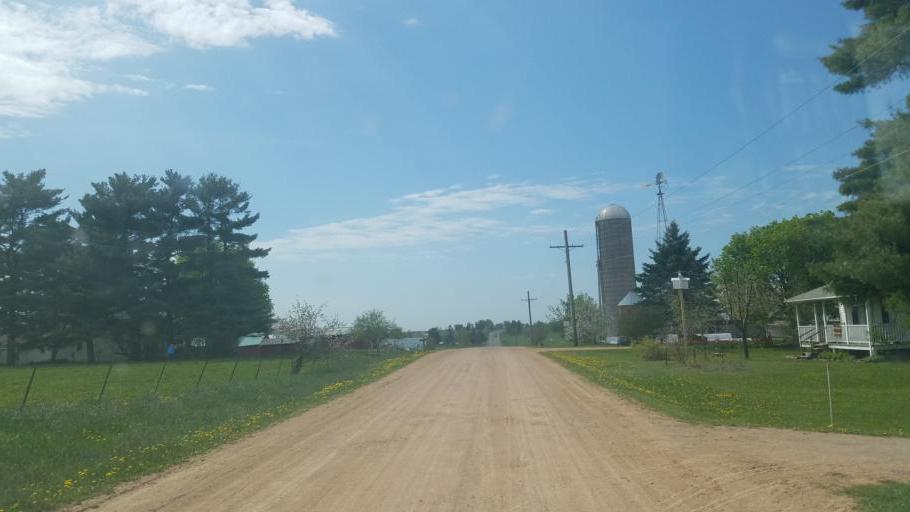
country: US
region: Wisconsin
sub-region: Marathon County
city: Spencer
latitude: 44.5967
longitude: -90.3763
